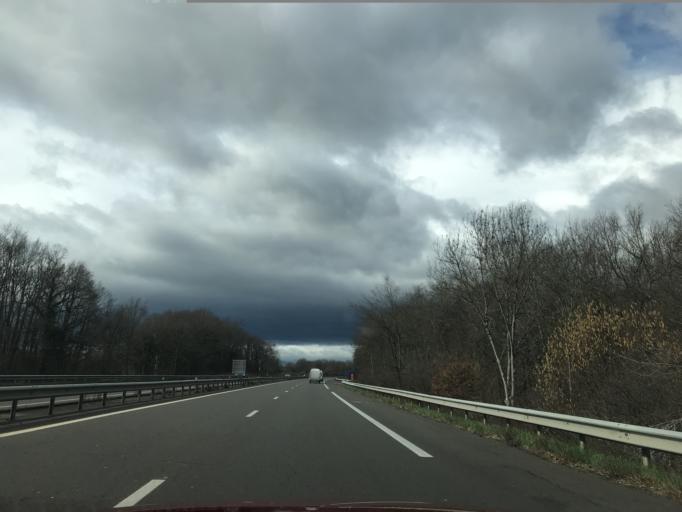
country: FR
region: Auvergne
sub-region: Departement du Puy-de-Dome
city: Lezoux
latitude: 45.8469
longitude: 3.3649
